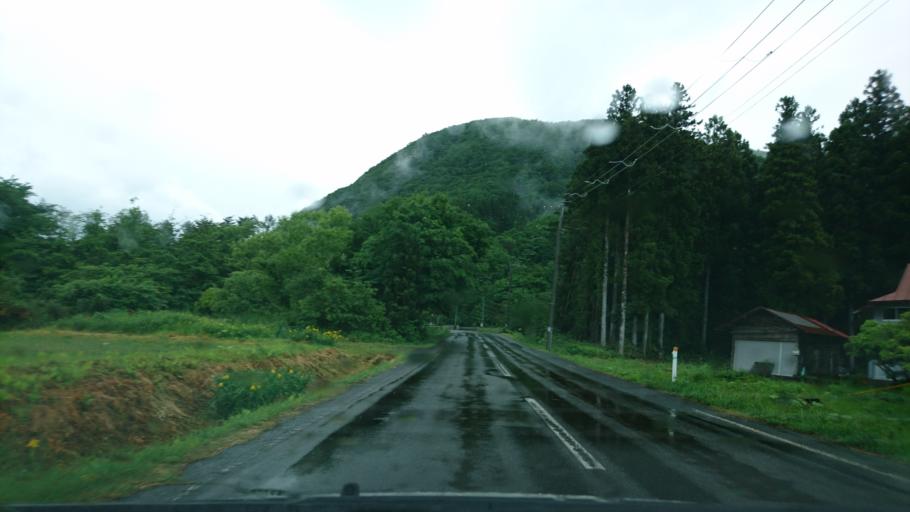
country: JP
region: Iwate
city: Ichinoseki
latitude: 38.9851
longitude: 140.9122
